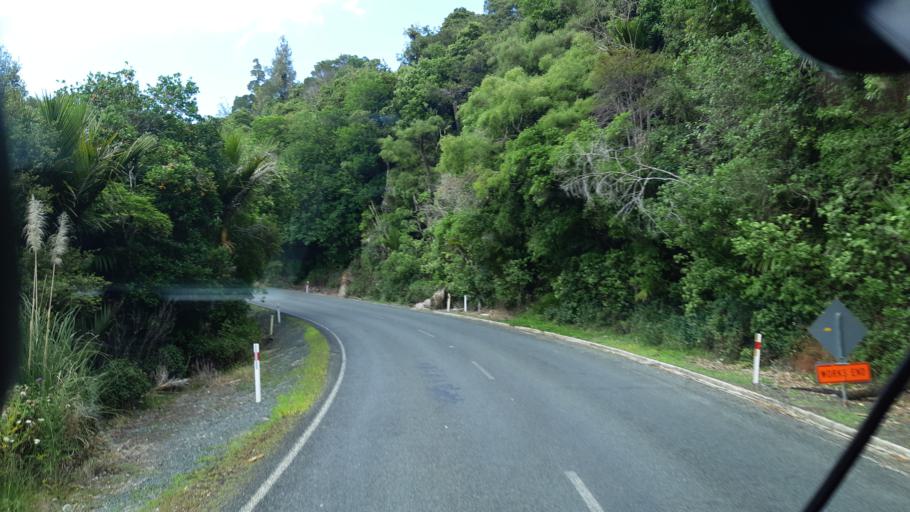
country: NZ
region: Northland
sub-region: Far North District
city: Taipa
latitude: -35.2466
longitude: 173.5312
